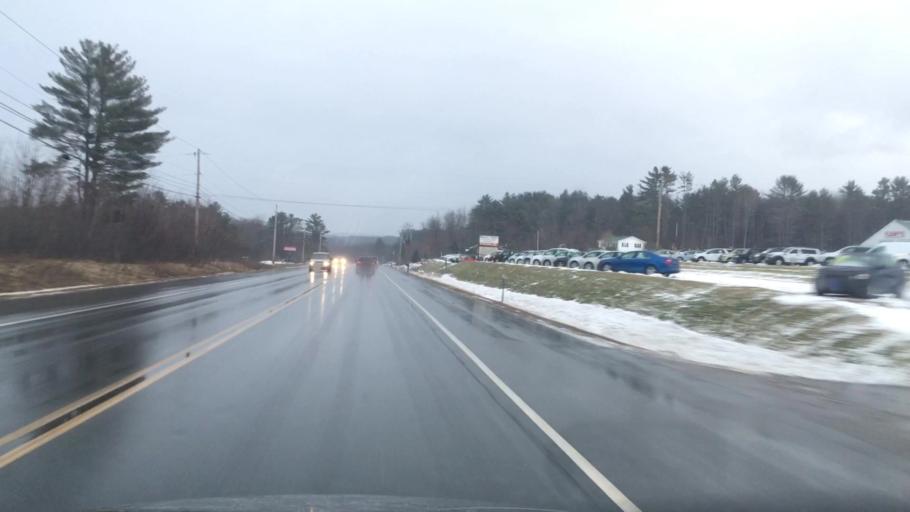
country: US
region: New Hampshire
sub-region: Sullivan County
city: Unity
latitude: 43.3665
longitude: -72.2513
